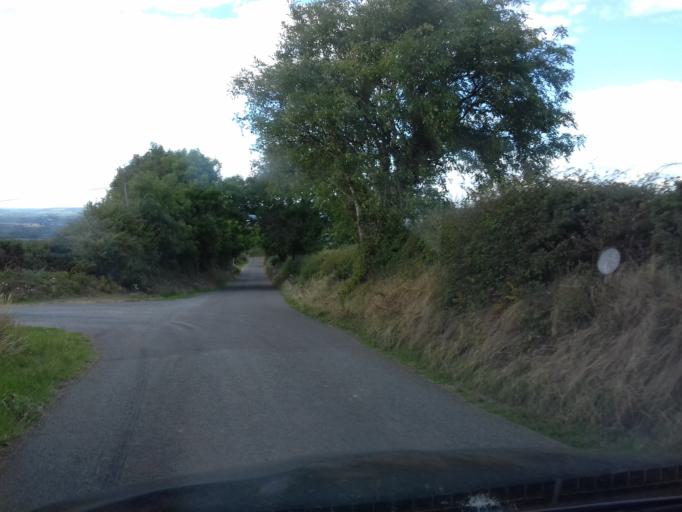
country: IE
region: Leinster
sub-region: Kilkenny
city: Graiguenamanagh
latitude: 52.5756
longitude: -7.0083
